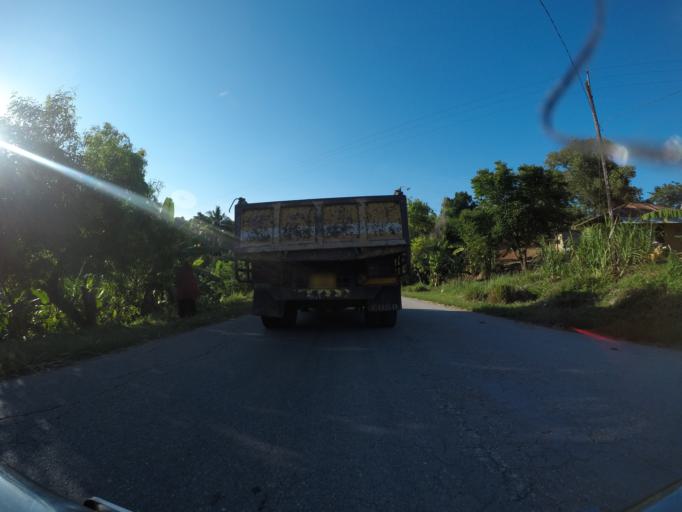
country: TZ
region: Pemba South
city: Uwelini
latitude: -5.3760
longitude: 39.6706
